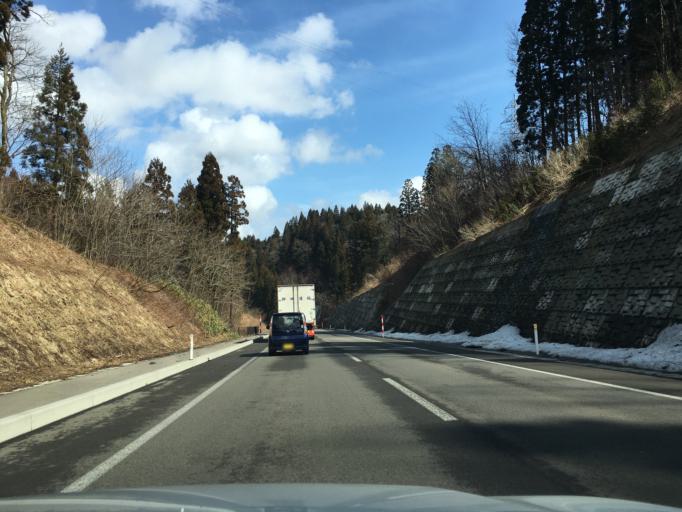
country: JP
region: Akita
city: Takanosu
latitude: 40.1119
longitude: 140.3690
